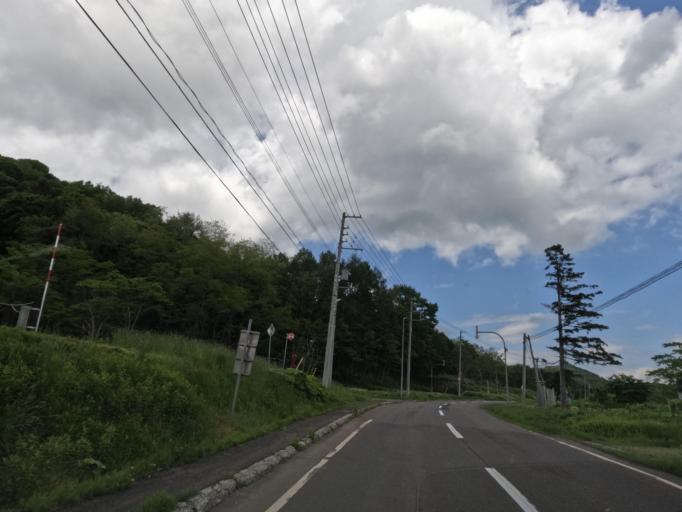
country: JP
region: Hokkaido
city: Takikawa
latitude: 43.5962
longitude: 141.7325
